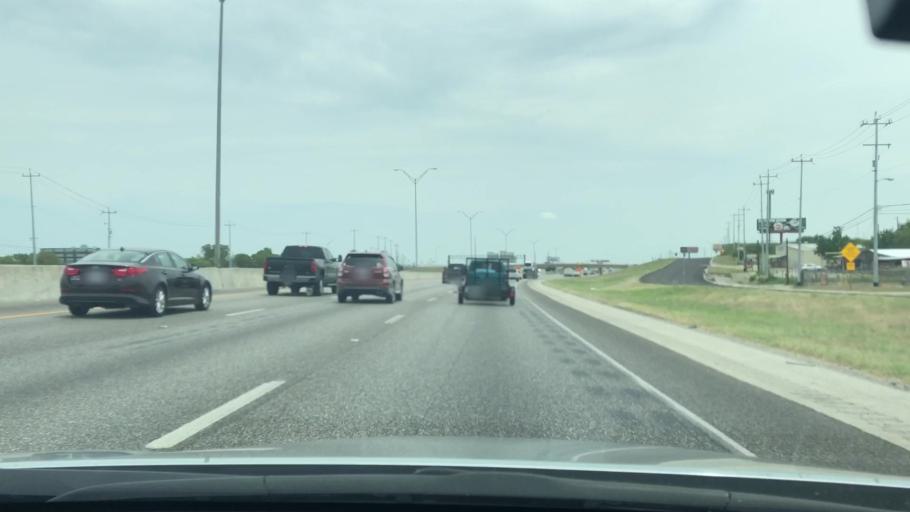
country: US
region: Texas
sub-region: Guadalupe County
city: Northcliff
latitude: 29.6139
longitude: -98.2604
